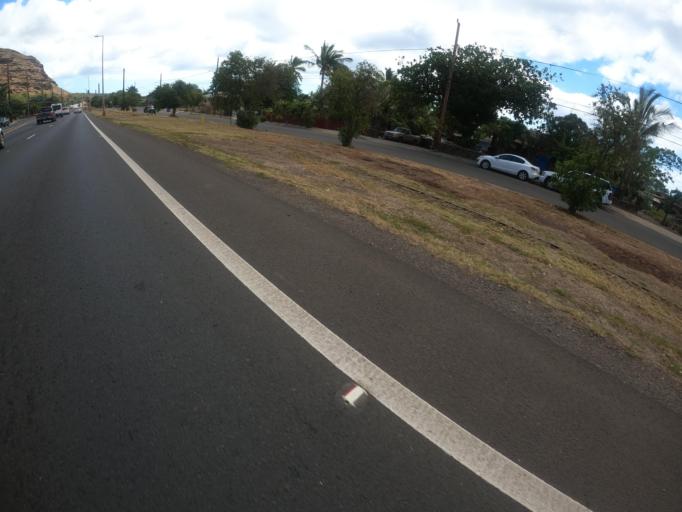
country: US
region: Hawaii
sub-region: Honolulu County
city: Nanakuli
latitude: 21.3736
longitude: -158.1393
